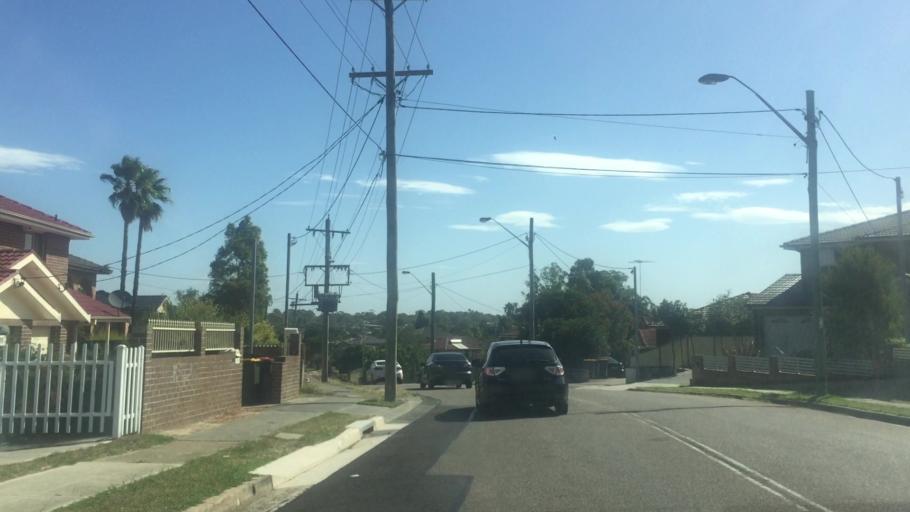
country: AU
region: New South Wales
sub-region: Holroyd
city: Merrylands
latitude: -33.8273
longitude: 150.9814
